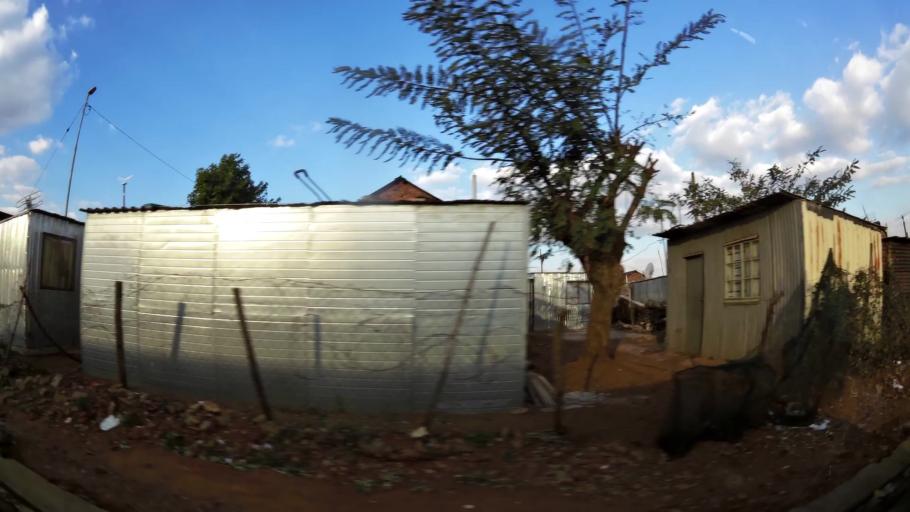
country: ZA
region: Gauteng
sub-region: West Rand District Municipality
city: Krugersdorp
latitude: -26.0783
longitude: 27.7578
